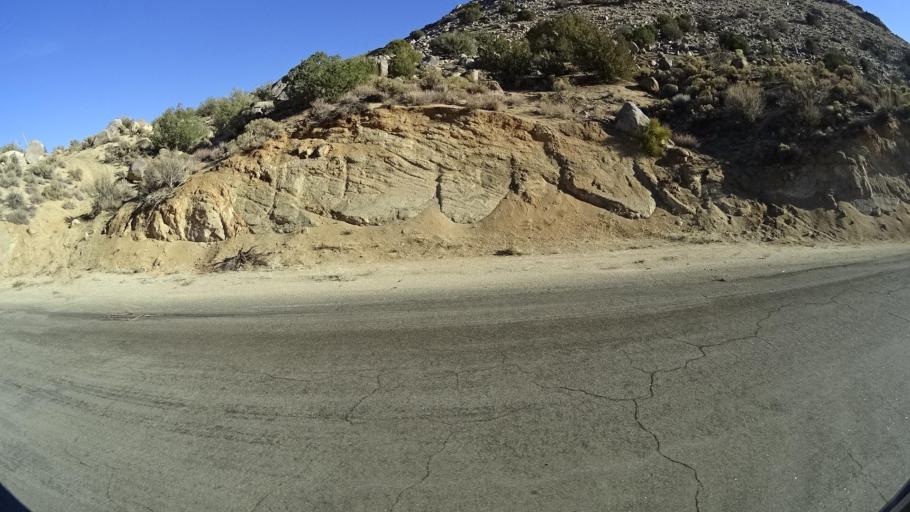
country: US
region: California
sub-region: Kern County
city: Weldon
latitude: 35.5805
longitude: -118.2492
